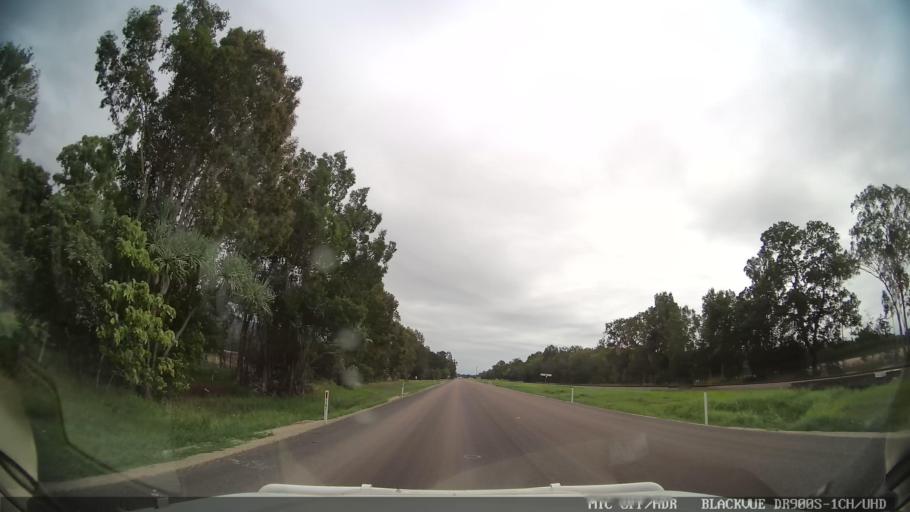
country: AU
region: Queensland
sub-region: Hinchinbrook
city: Ingham
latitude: -18.9319
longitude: 146.2677
